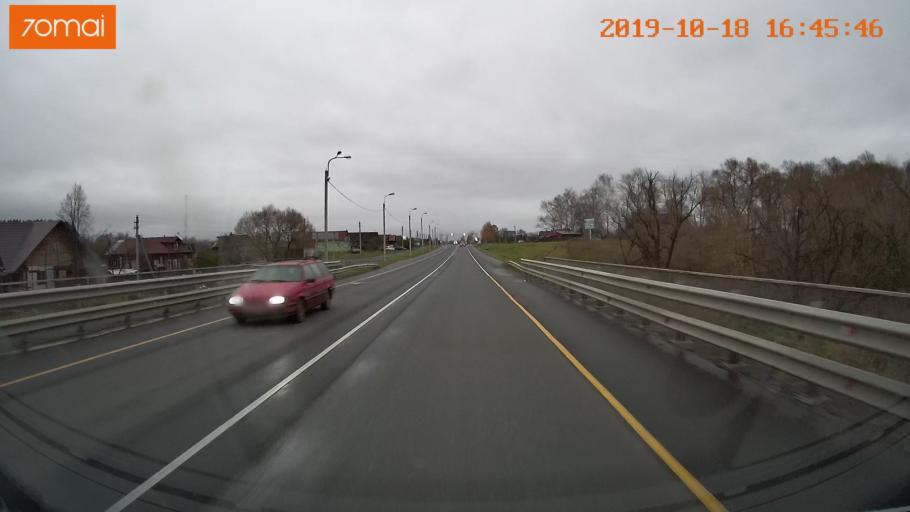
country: RU
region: Vladimir
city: Kideksha
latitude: 56.5109
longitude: 40.5479
